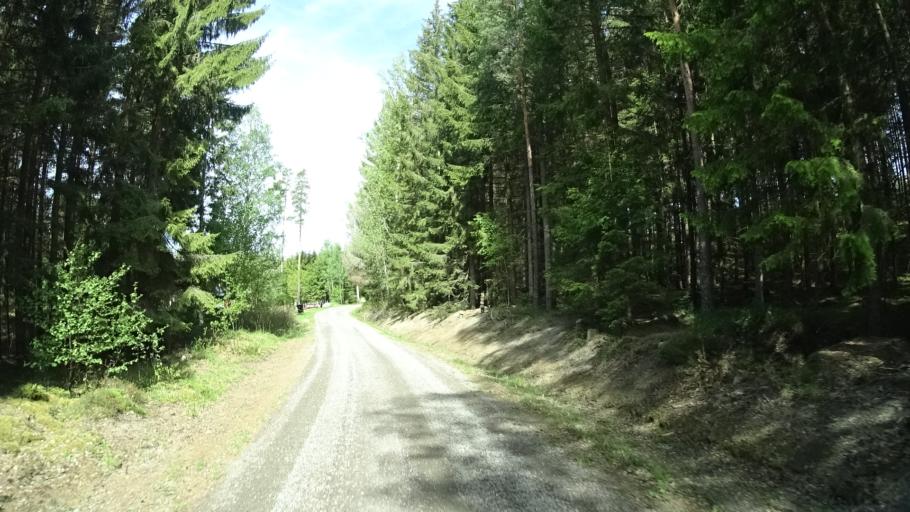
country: SE
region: OEstergoetland
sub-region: Finspangs Kommun
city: Finspang
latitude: 58.7926
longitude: 15.8617
